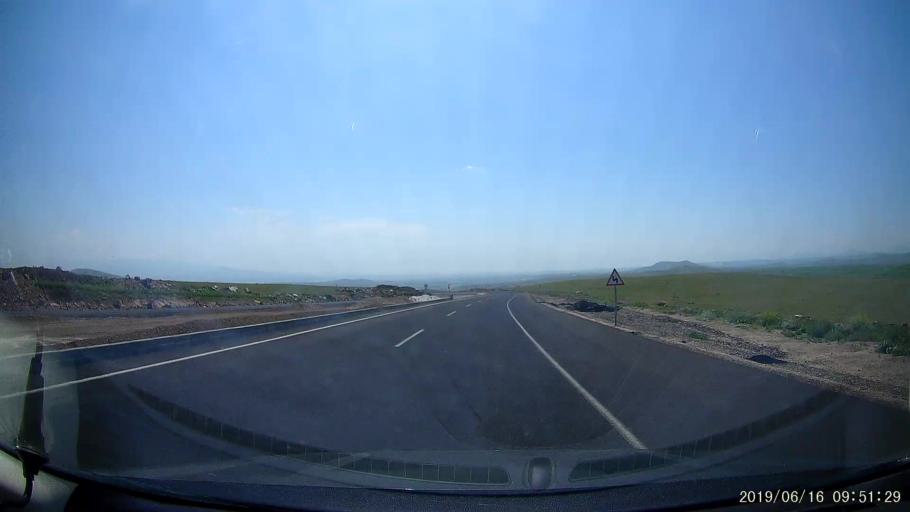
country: TR
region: Kars
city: Digor
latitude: 40.3912
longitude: 43.3677
